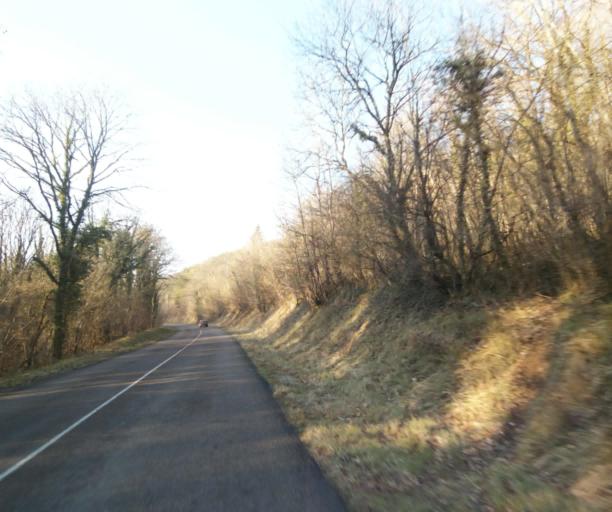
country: FR
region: Champagne-Ardenne
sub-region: Departement de la Haute-Marne
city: Bienville
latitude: 48.5639
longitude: 5.0624
